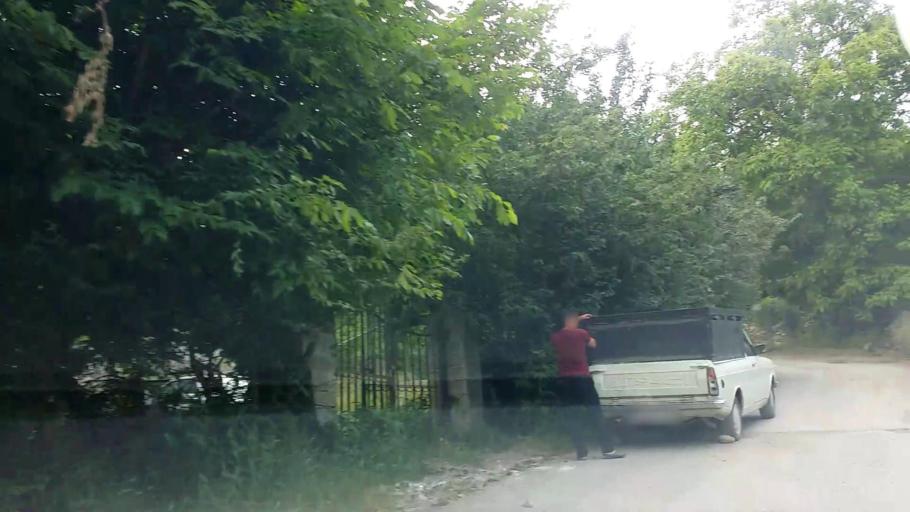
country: IR
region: Mazandaran
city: Chalus
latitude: 36.5551
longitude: 51.2723
